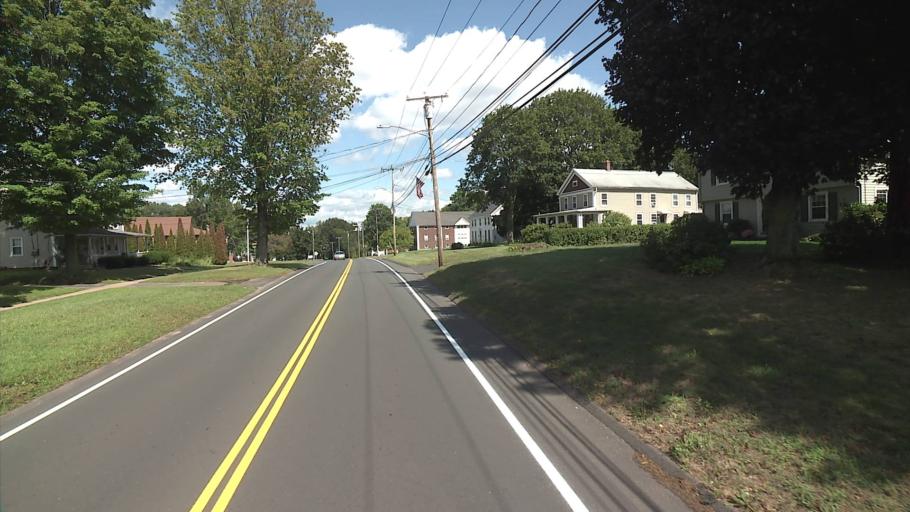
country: US
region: Connecticut
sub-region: Middlesex County
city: Cromwell
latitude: 41.5924
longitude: -72.6230
